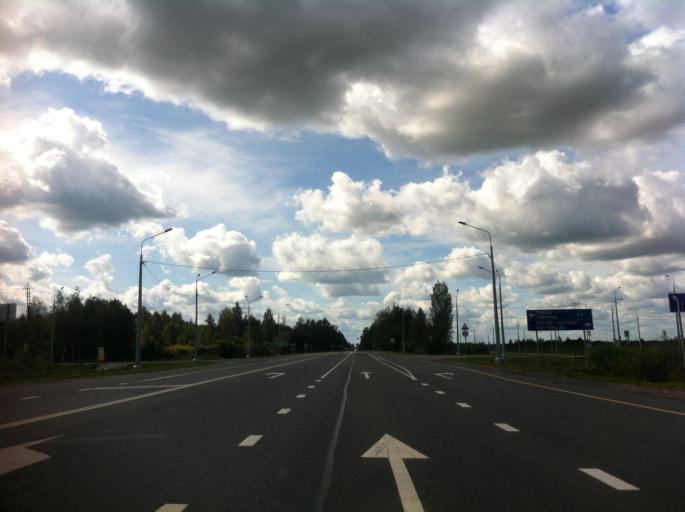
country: RU
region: Pskov
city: Pskov
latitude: 57.7711
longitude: 28.1291
